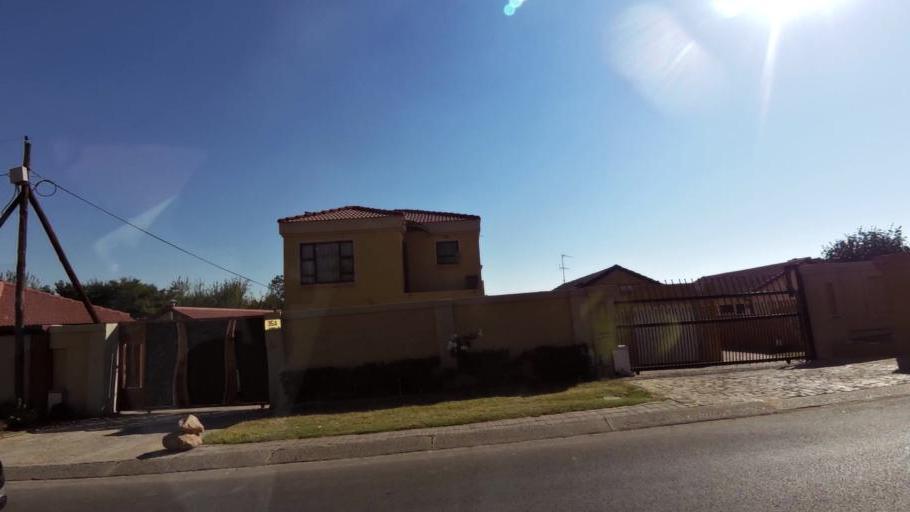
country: ZA
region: Gauteng
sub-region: City of Johannesburg Metropolitan Municipality
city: Johannesburg
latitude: -26.2524
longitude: 27.9905
